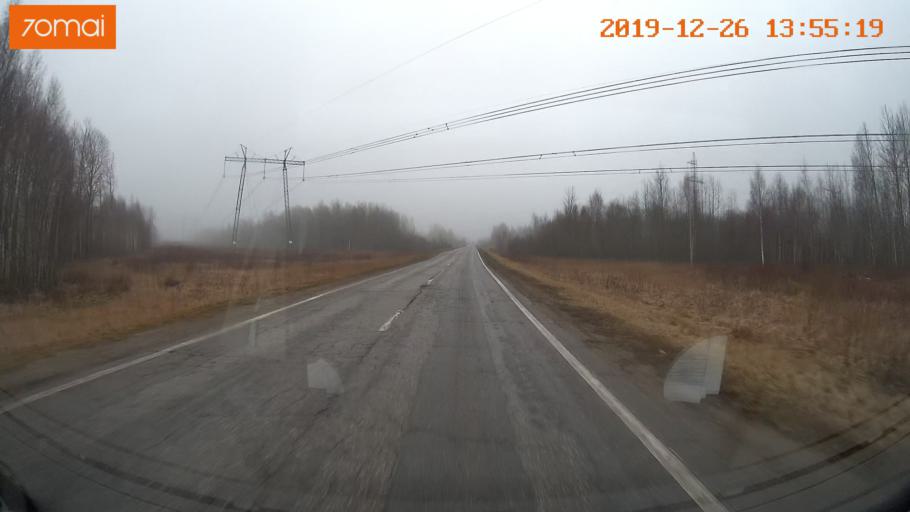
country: RU
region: Jaroslavl
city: Poshekhon'ye
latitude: 58.6050
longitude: 38.6455
